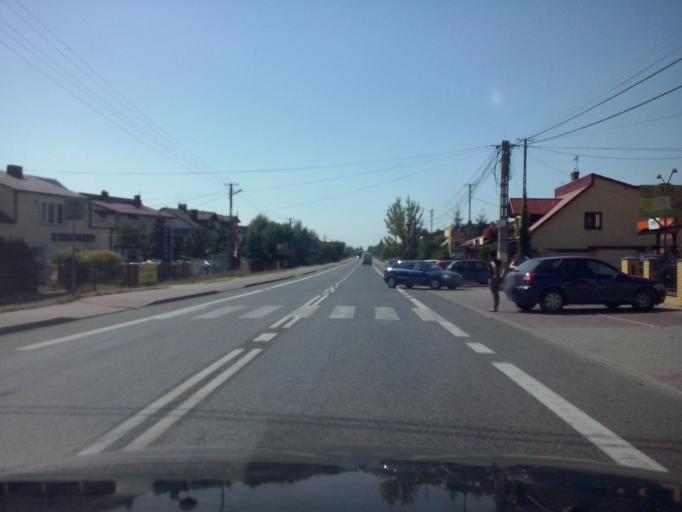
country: PL
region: Swietokrzyskie
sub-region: Powiat kielecki
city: Bieliny
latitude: 50.8496
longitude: 20.9367
